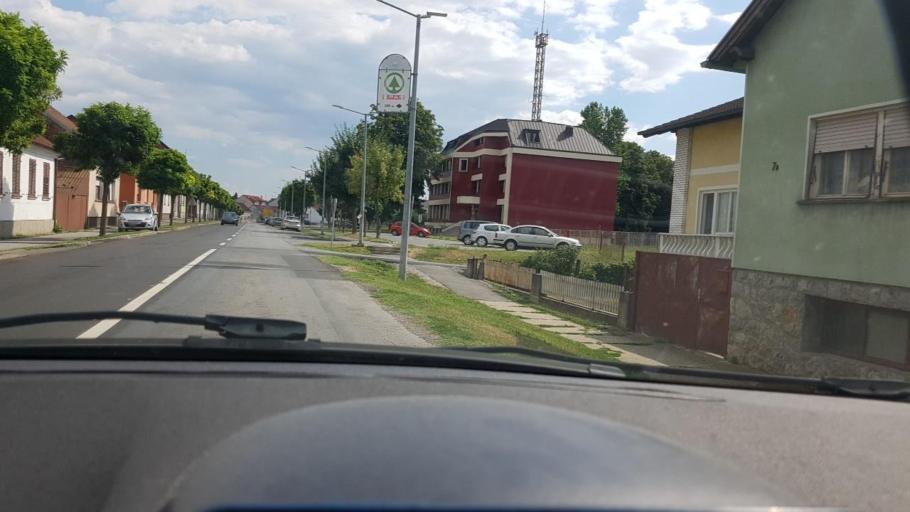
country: HR
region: Bjelovarsko-Bilogorska
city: Bjelovar
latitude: 45.9075
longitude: 16.8467
